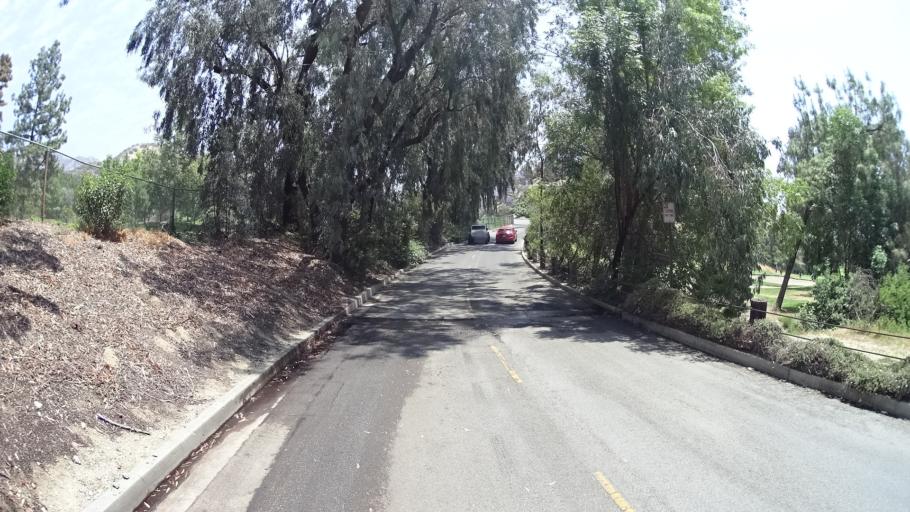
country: US
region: California
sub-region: Los Angeles County
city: Burbank
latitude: 34.2061
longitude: -118.3041
